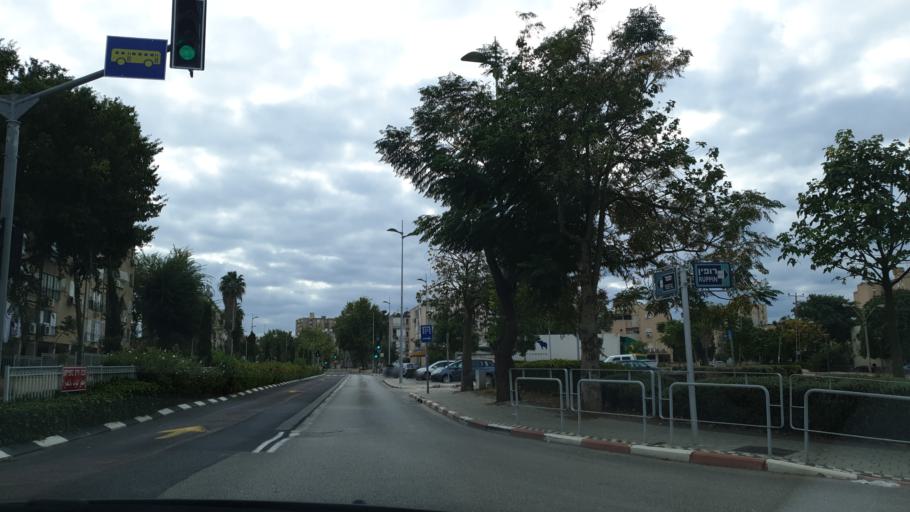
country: IL
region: Haifa
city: Qiryat Ata
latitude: 32.8167
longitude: 35.1134
